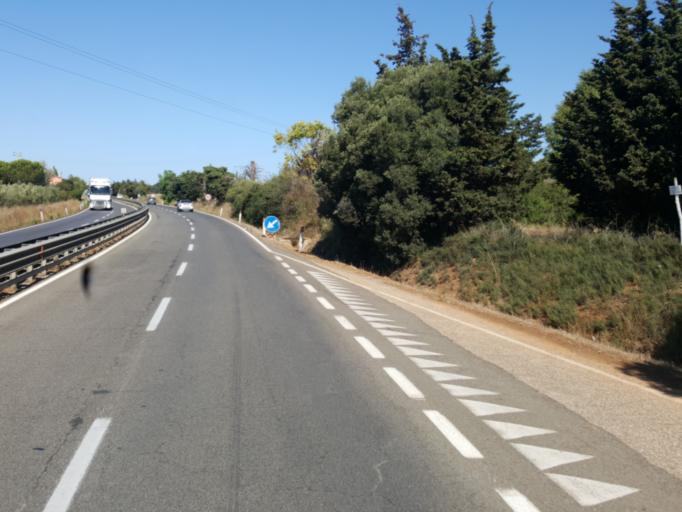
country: IT
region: Tuscany
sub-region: Provincia di Grosseto
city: Orbetello Scalo
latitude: 42.4374
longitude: 11.2777
